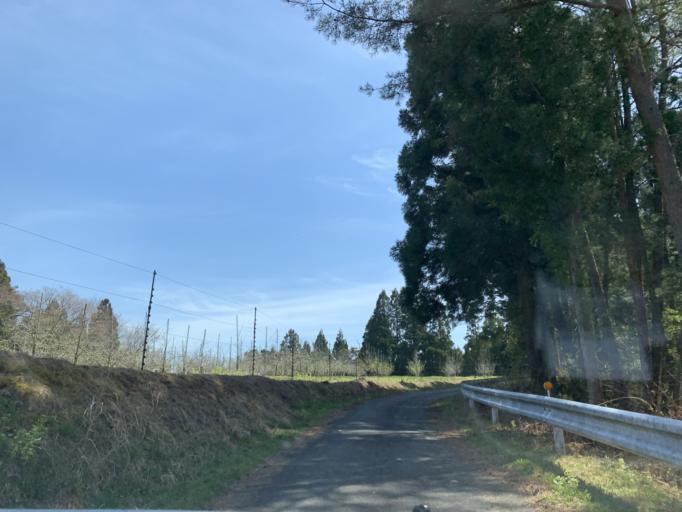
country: JP
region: Iwate
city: Ichinoseki
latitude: 38.8360
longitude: 141.2883
